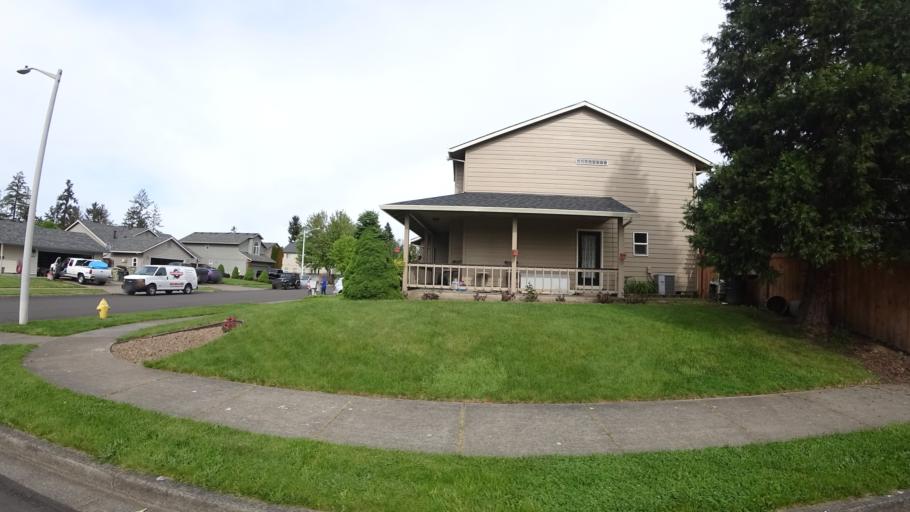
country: US
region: Oregon
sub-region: Washington County
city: Aloha
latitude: 45.5075
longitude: -122.9209
